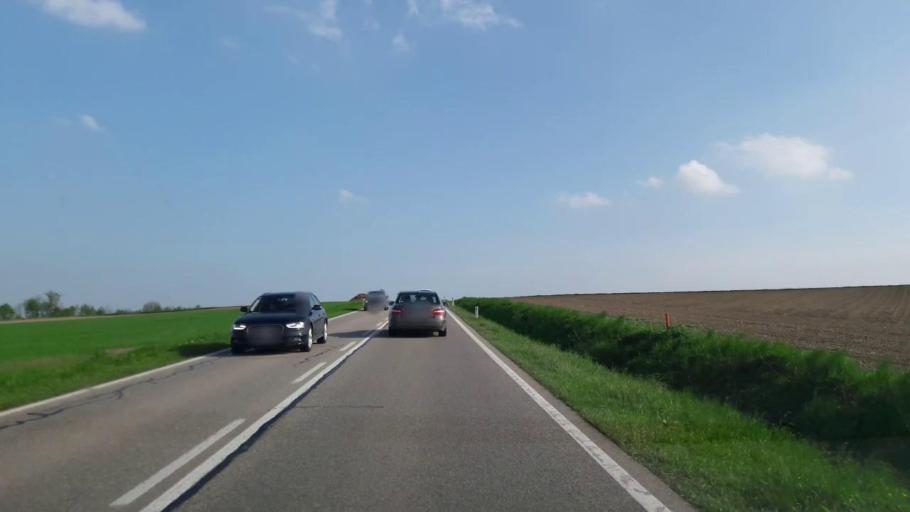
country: AT
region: Lower Austria
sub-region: Politischer Bezirk Hollabrunn
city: Guntersdorf
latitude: 48.6223
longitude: 16.0654
